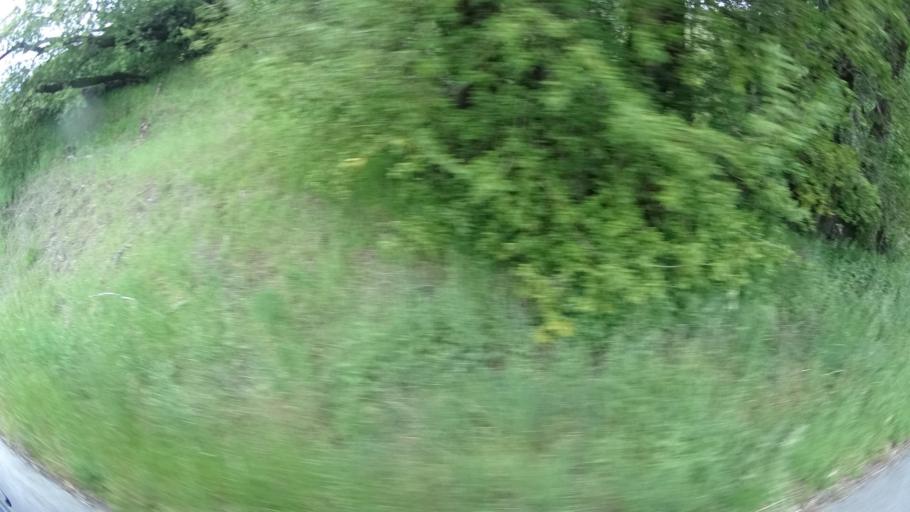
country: US
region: California
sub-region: Humboldt County
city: Redway
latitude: 40.1121
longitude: -123.7713
